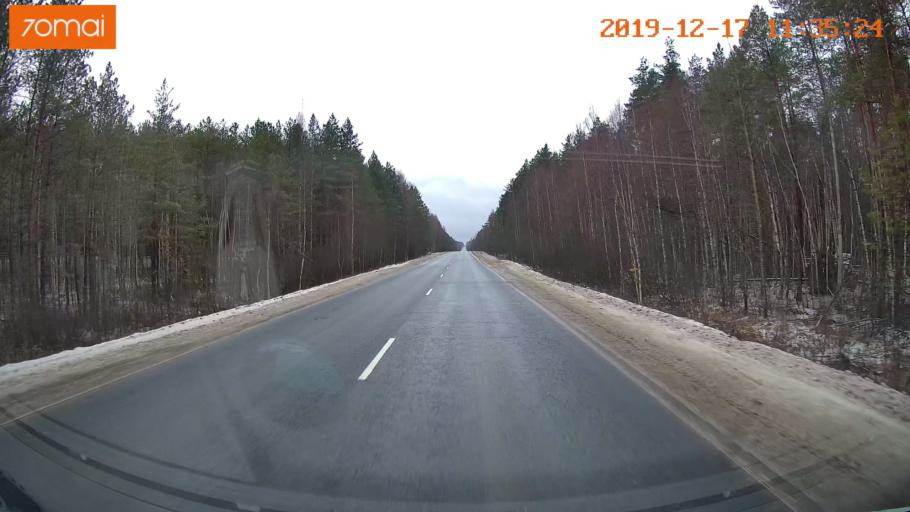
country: RU
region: Vladimir
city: Velikodvorskiy
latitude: 55.3885
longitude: 40.6828
